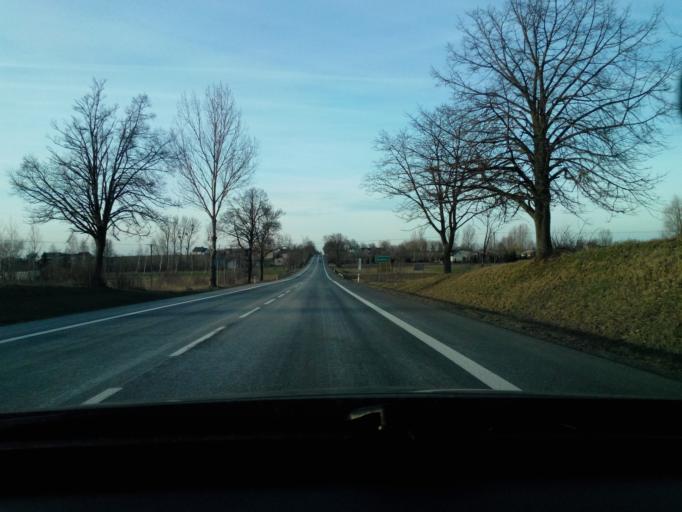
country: PL
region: Kujawsko-Pomorskie
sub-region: Powiat wloclawski
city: Lubien Kujawski
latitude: 52.4413
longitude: 19.1607
